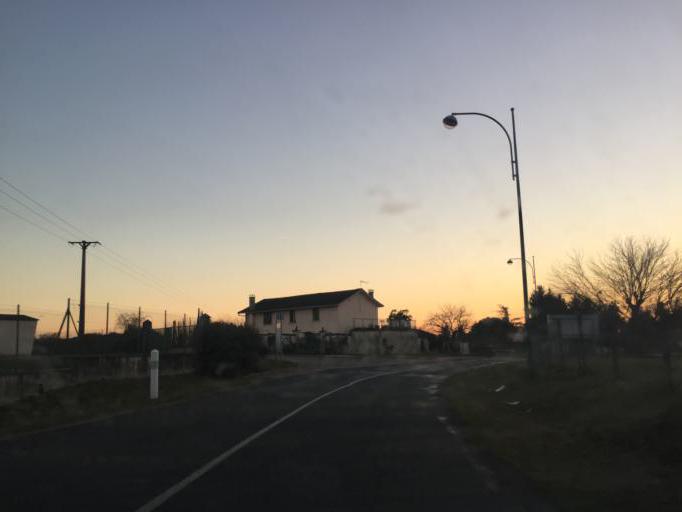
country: FR
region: Rhone-Alpes
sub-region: Departement de l'Ain
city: Balan
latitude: 45.8434
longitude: 5.1140
